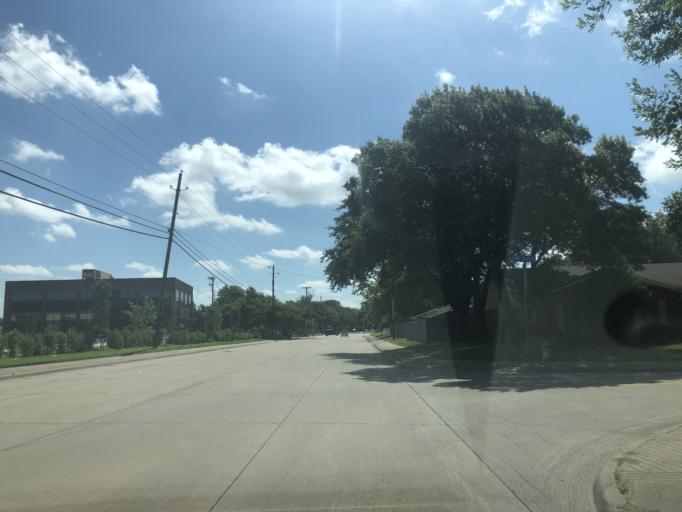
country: US
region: Texas
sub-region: Dallas County
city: Duncanville
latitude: 32.6551
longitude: -96.9276
